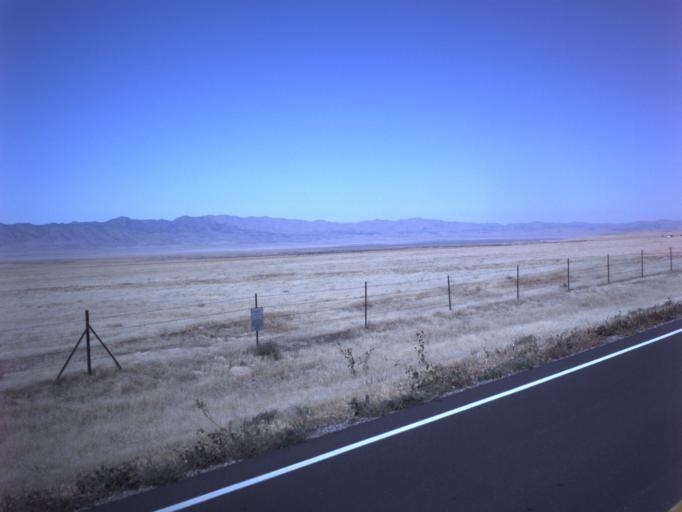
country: US
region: Utah
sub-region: Tooele County
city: Grantsville
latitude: 40.3839
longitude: -112.7470
